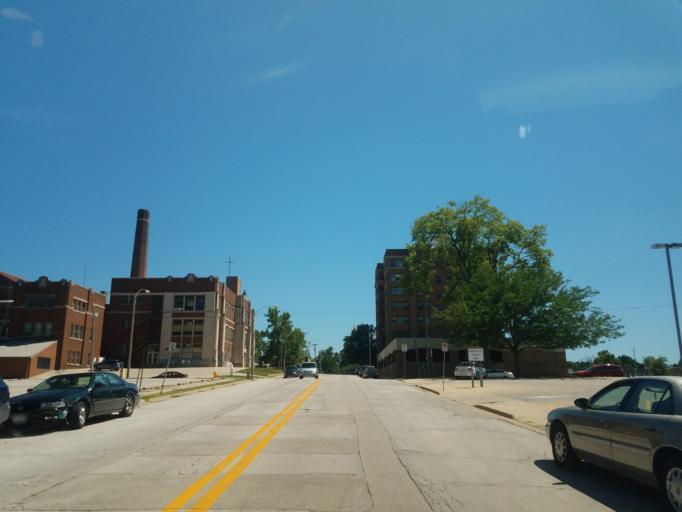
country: US
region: Illinois
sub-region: McLean County
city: Bloomington
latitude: 40.4809
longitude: -88.9886
